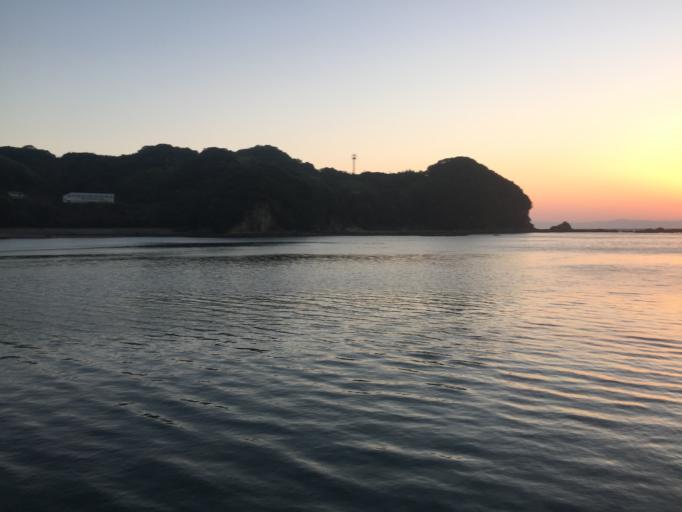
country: JP
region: Nagasaki
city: Nagasaki-shi
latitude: 32.7069
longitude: 129.9144
